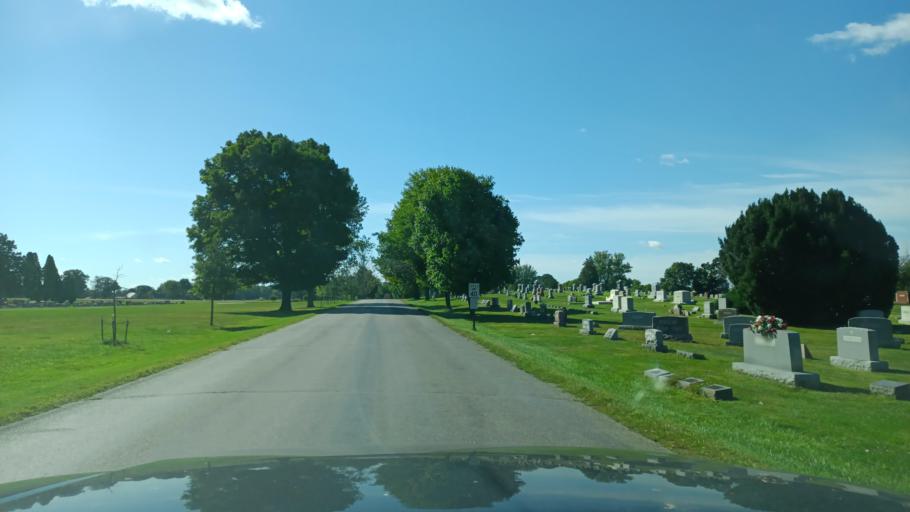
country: US
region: Indiana
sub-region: Fountain County
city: Covington
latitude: 40.1324
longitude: -87.3860
